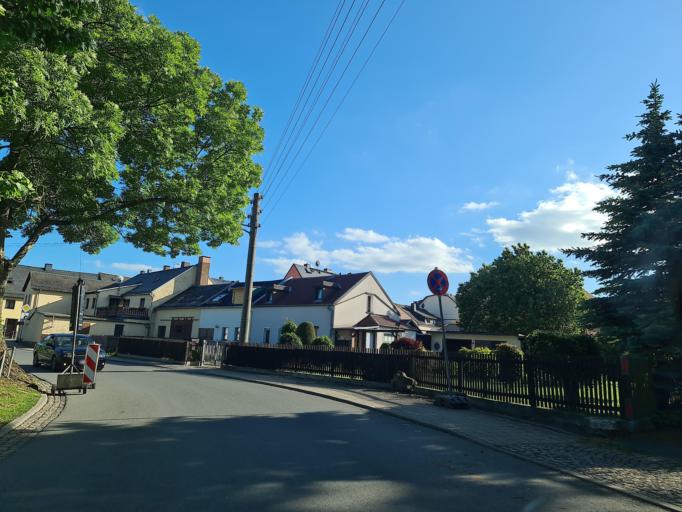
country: DE
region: Saxony
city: Weischlitz
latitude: 50.4926
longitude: 12.0885
